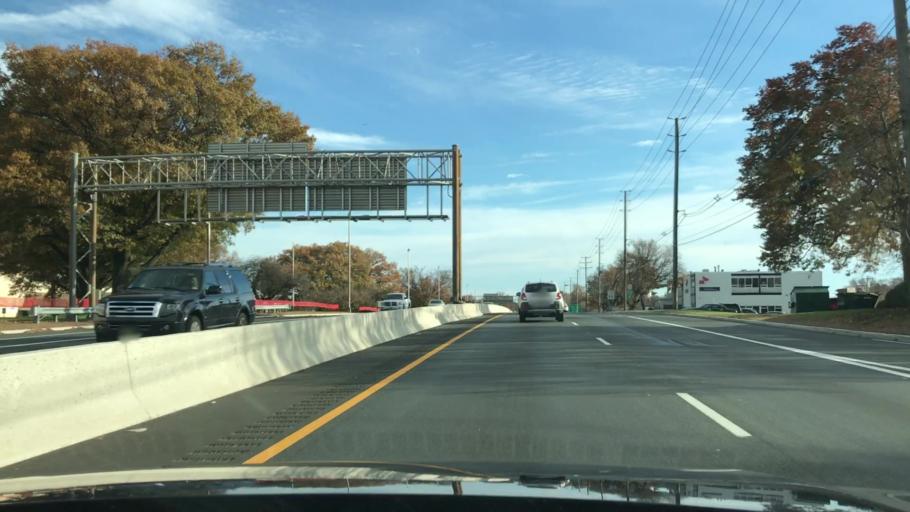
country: US
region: New Jersey
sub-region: Bergen County
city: Fair Lawn
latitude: 40.9490
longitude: -74.1360
